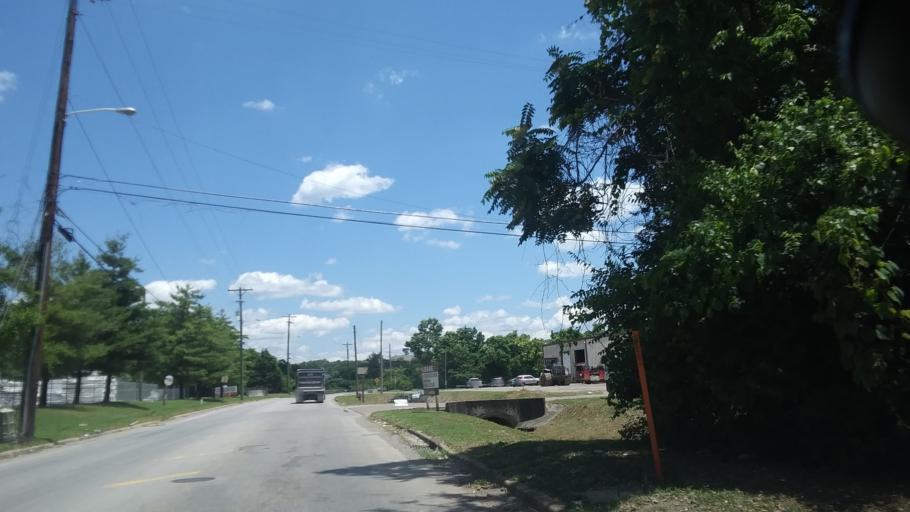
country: US
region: Tennessee
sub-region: Davidson County
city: Oak Hill
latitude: 36.0812
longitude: -86.6827
